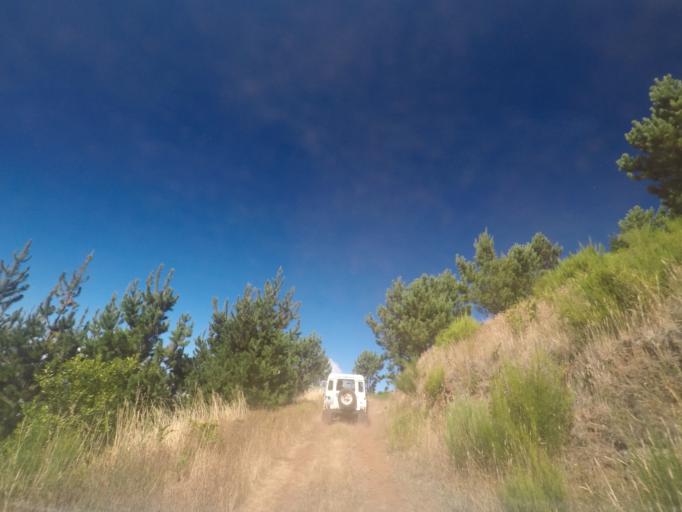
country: PT
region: Madeira
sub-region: Funchal
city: Nossa Senhora do Monte
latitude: 32.7066
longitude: -16.9087
